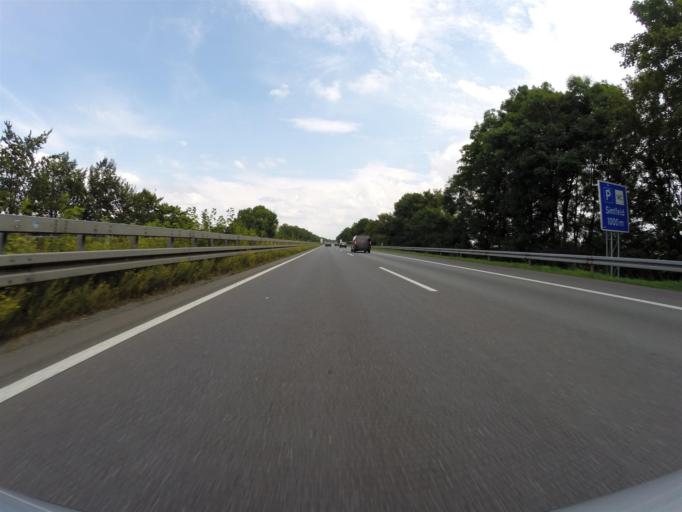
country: DE
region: North Rhine-Westphalia
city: Marsberg
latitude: 51.5520
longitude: 8.8074
